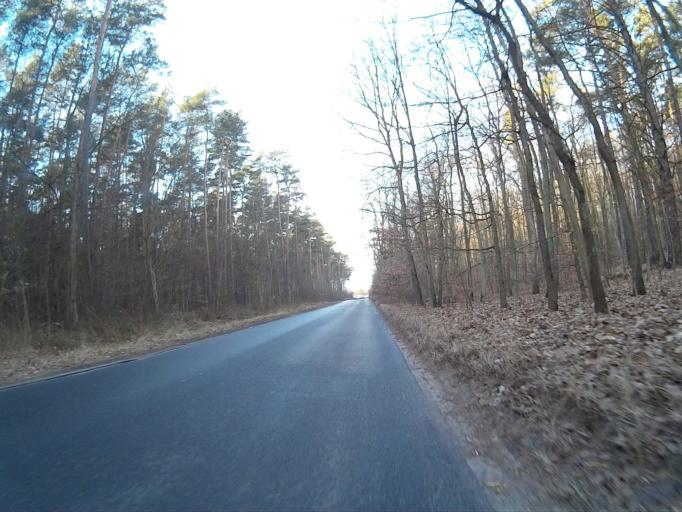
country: PL
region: Kujawsko-Pomorskie
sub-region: Powiat bydgoski
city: Osielsko
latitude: 53.1615
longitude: 18.0613
